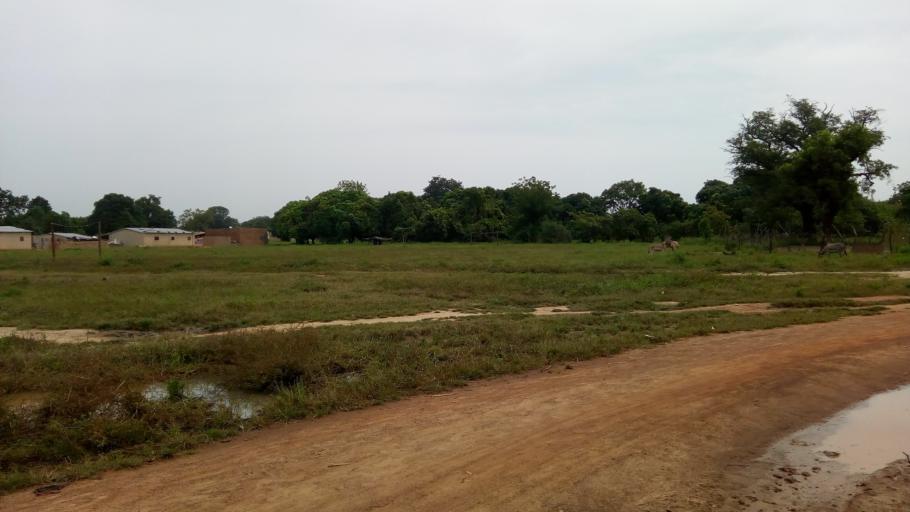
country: ML
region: Koulikoro
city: Kangaba
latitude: 11.6836
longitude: -8.6940
